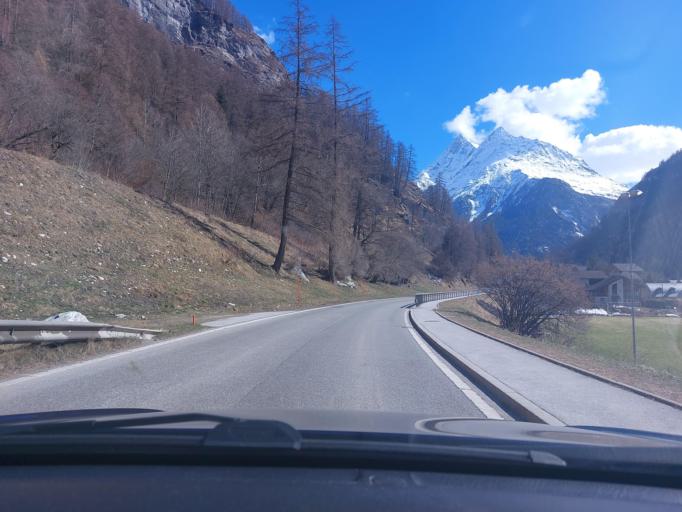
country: CH
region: Valais
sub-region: Herens District
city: Evolene
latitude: 46.1127
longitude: 7.4993
